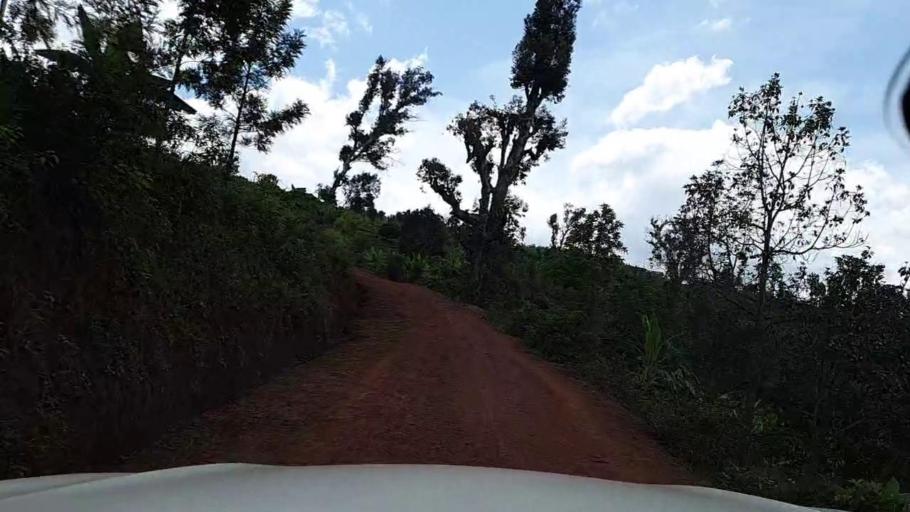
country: RW
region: Southern Province
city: Butare
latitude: -2.7499
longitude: 29.7622
